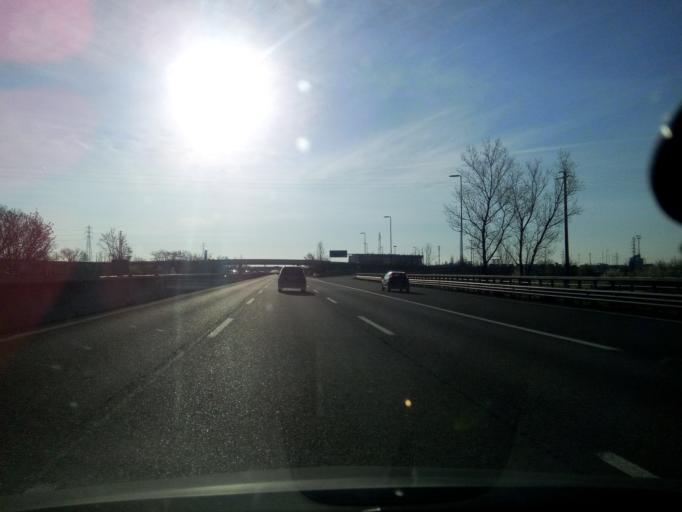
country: IT
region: Emilia-Romagna
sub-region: Provincia di Parma
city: Baganzola
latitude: 44.8414
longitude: 10.3325
